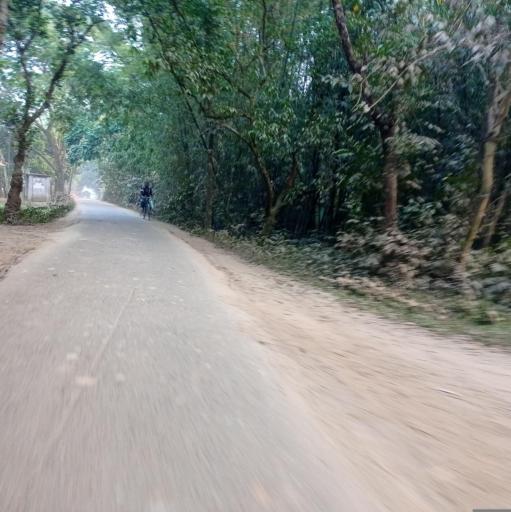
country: BD
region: Dhaka
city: Bajitpur
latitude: 24.1317
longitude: 90.8191
